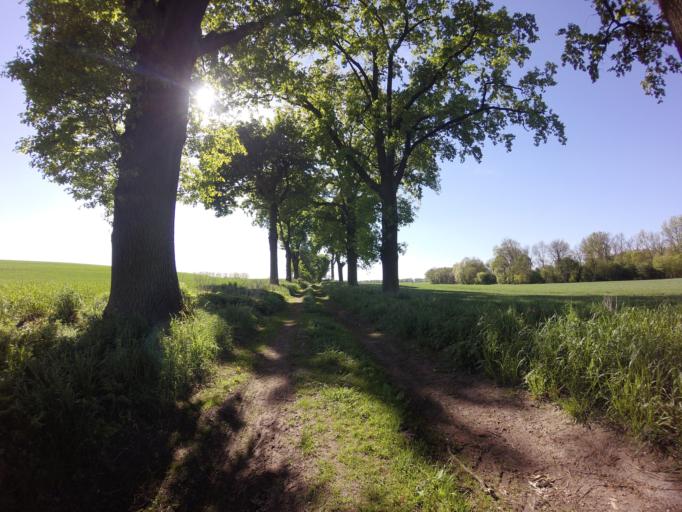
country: PL
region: West Pomeranian Voivodeship
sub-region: Powiat choszczenski
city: Choszczno
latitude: 53.1571
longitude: 15.3097
